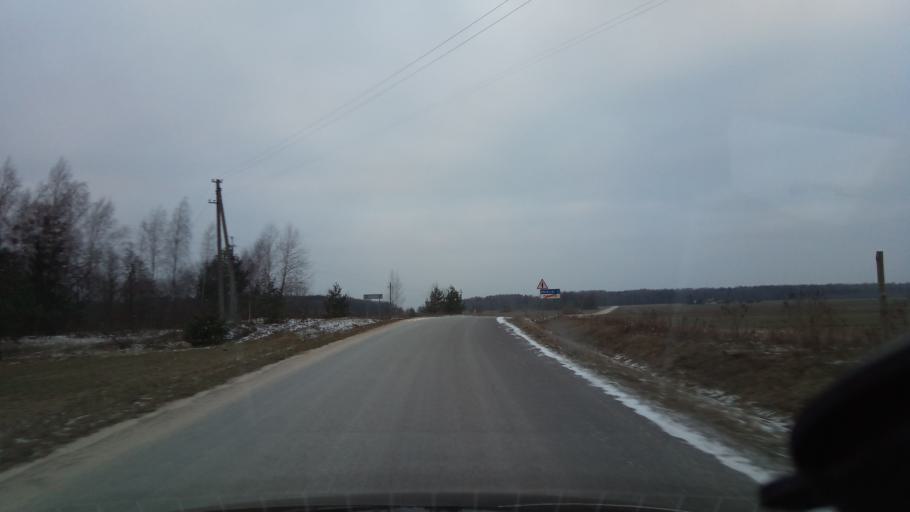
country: LT
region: Alytaus apskritis
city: Varena
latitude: 54.1168
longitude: 24.7434
